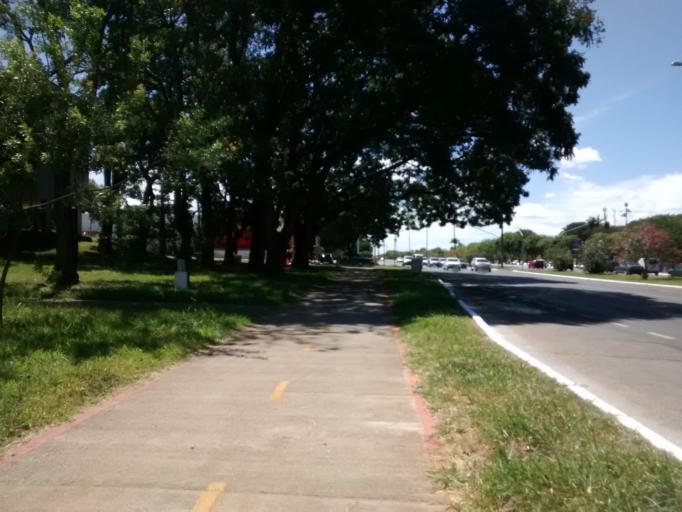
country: BR
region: Federal District
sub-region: Brasilia
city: Brasilia
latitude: -15.8159
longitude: -47.8898
